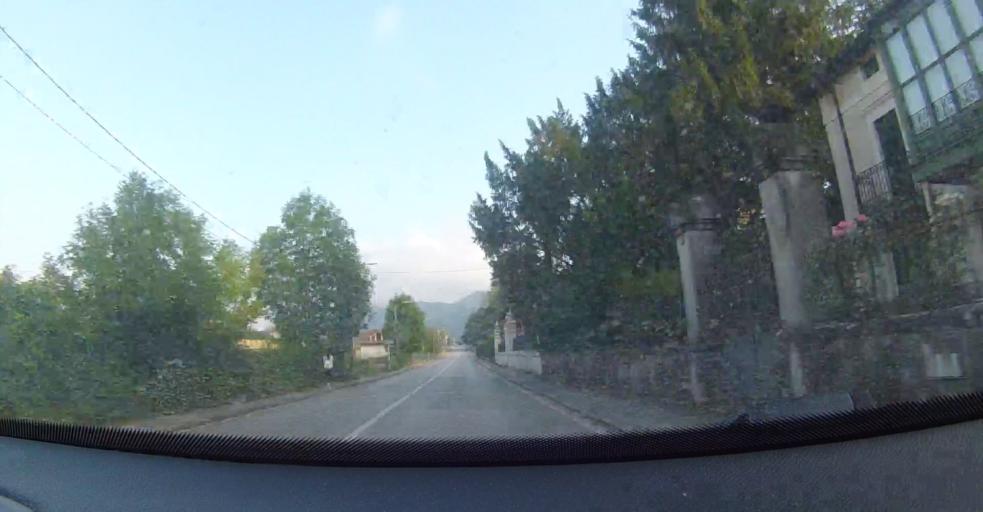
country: ES
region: Basque Country
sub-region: Bizkaia
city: Sopuerta
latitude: 43.2719
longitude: -3.1553
